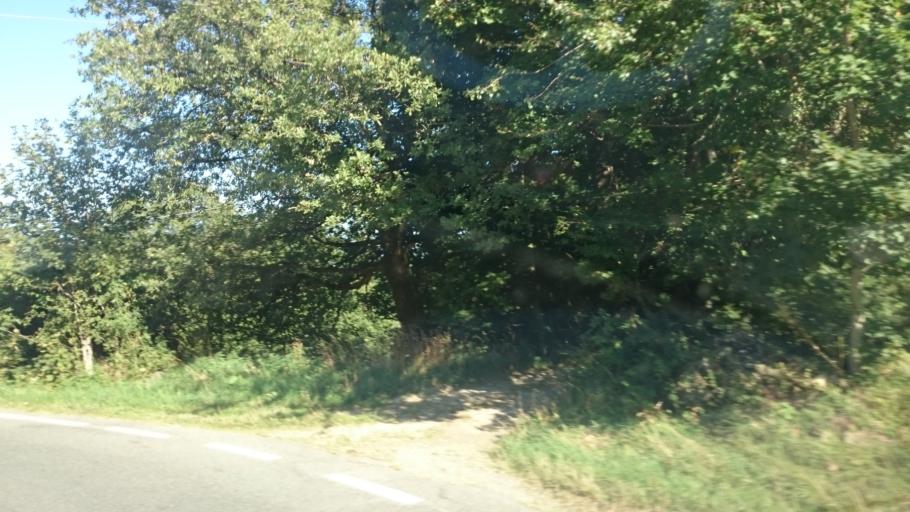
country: IT
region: Emilia-Romagna
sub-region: Provincia di Reggio Emilia
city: Villa Minozzo
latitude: 44.3042
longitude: 10.4323
